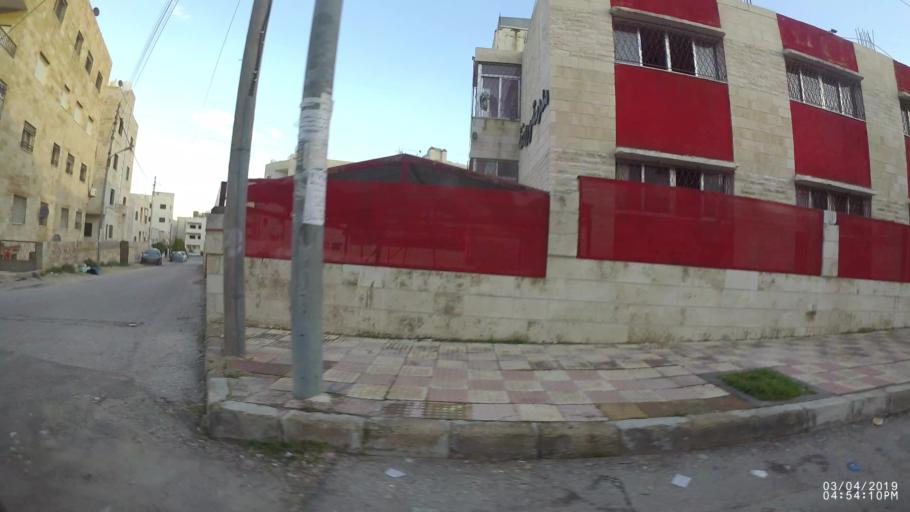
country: JO
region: Amman
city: Al Bunayyat ash Shamaliyah
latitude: 31.9171
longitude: 35.8936
